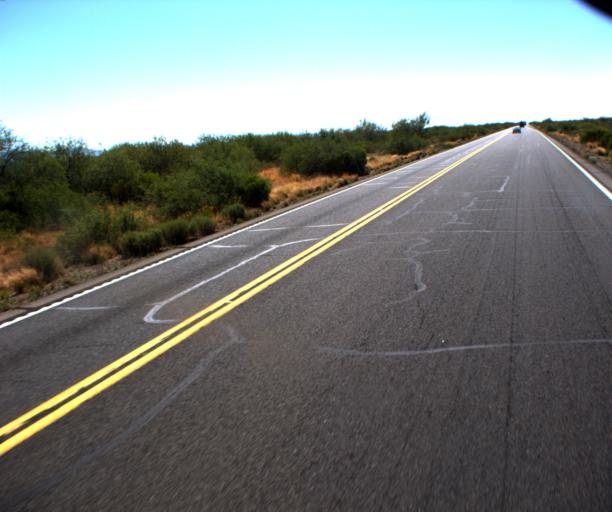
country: US
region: Arizona
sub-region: Yavapai County
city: Congress
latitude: 34.1446
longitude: -112.9810
